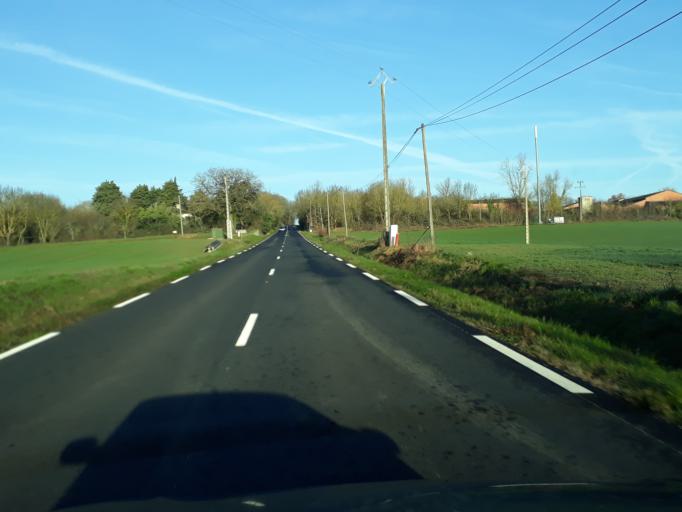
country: FR
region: Midi-Pyrenees
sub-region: Departement du Gers
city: Pujaudran
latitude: 43.5532
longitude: 1.1418
